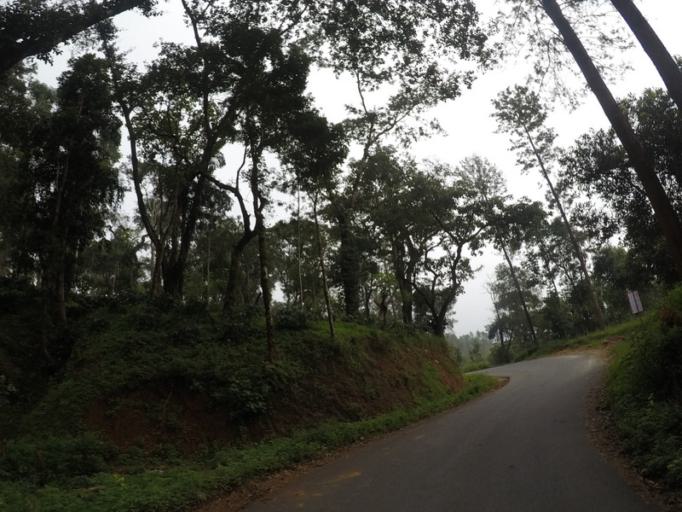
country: IN
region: Karnataka
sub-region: Chikmagalur
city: Mudigere
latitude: 13.1692
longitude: 75.4651
